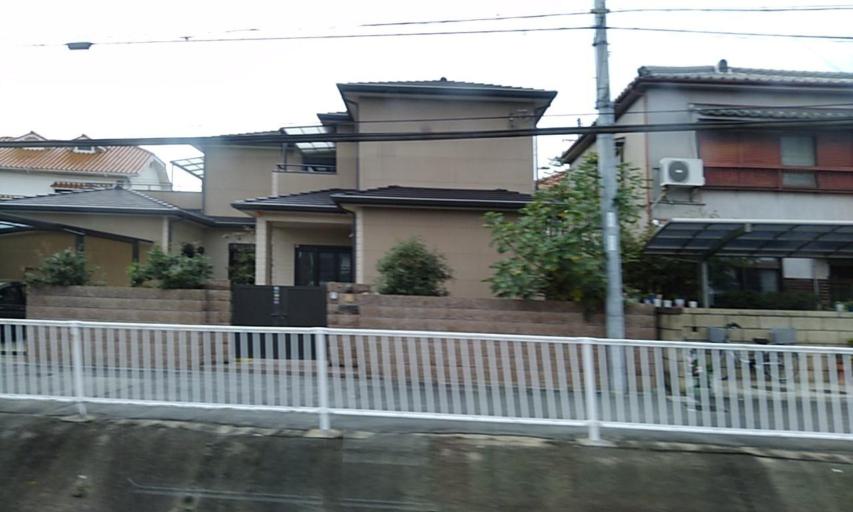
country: JP
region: Osaka
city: Matsubara
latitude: 34.5724
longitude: 135.5752
